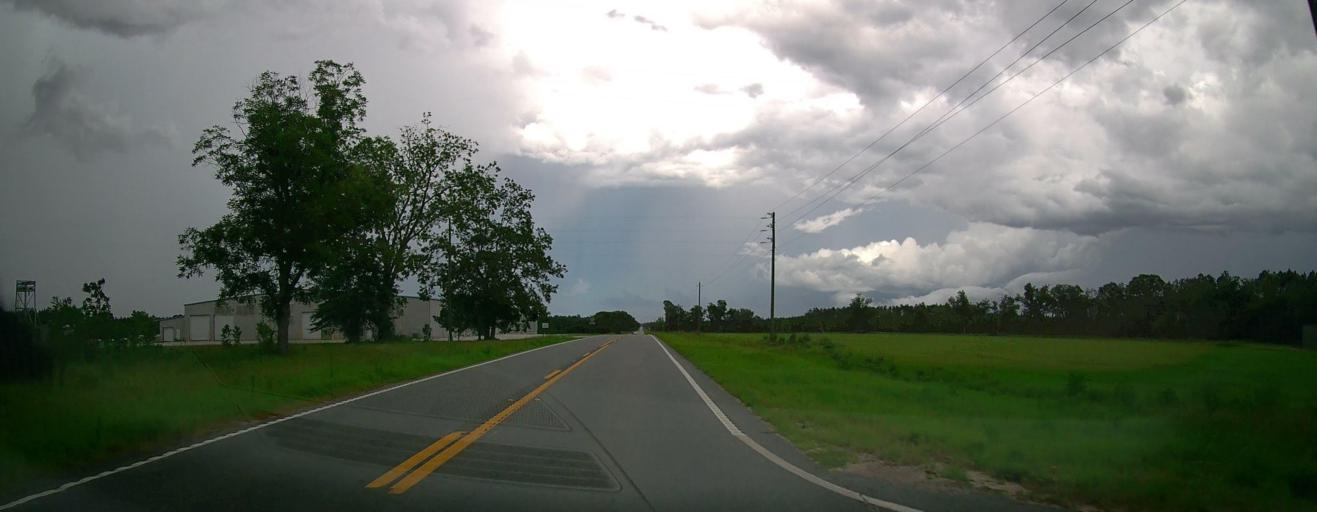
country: US
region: Georgia
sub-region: Pierce County
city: Blackshear
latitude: 31.3734
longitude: -82.1112
